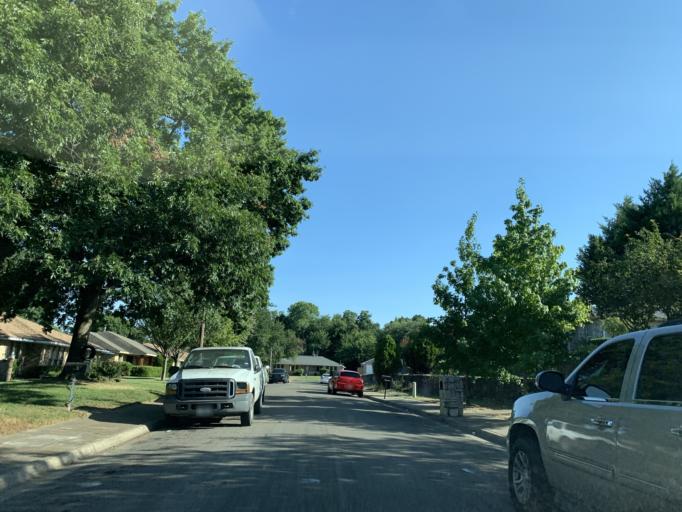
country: US
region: Texas
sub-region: Dallas County
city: Cockrell Hill
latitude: 32.7085
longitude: -96.8841
